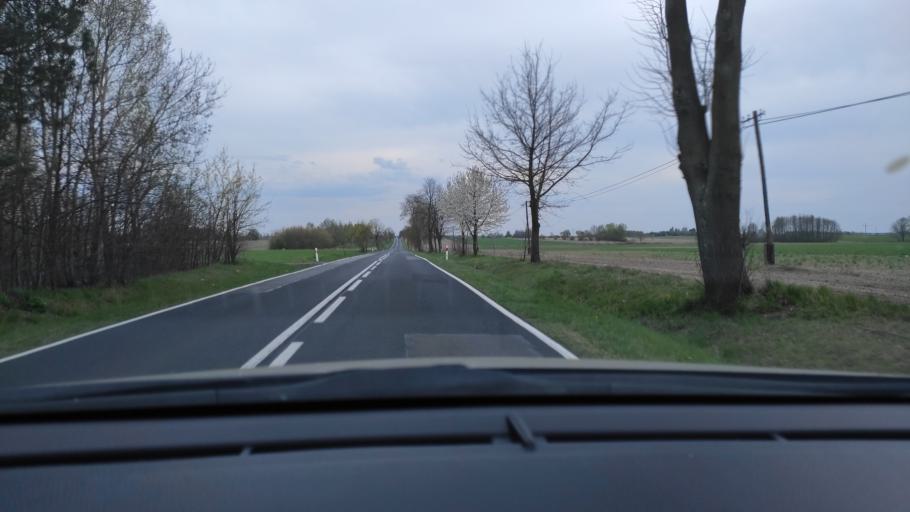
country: PL
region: Masovian Voivodeship
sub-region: Powiat zwolenski
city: Zwolen
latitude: 51.3780
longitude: 21.5627
